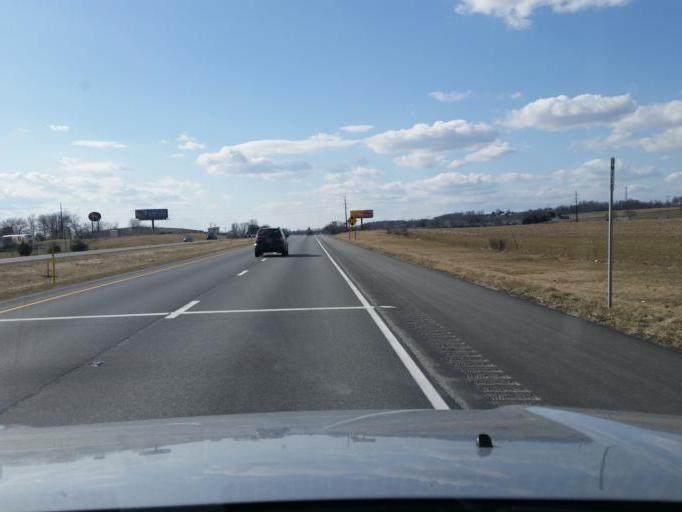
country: US
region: Pennsylvania
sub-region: Lancaster County
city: Salunga
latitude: 40.1193
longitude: -76.4583
